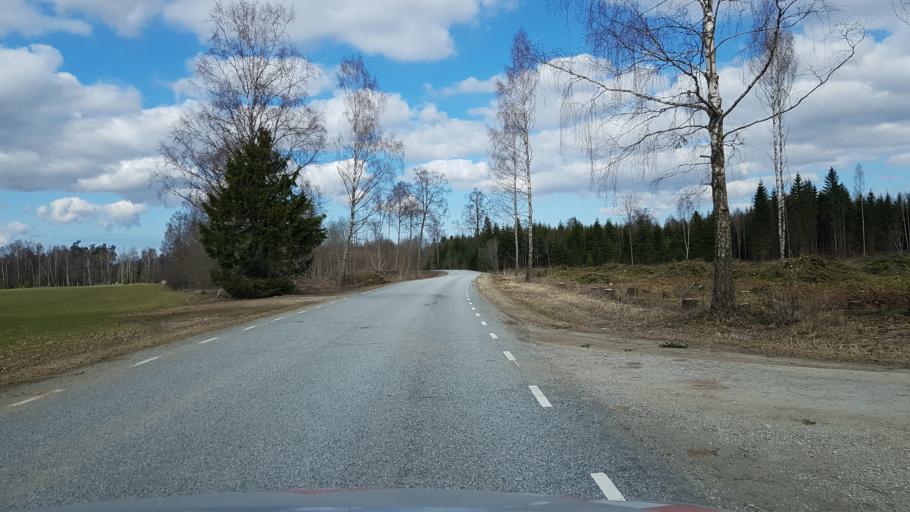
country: EE
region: Laeaene-Virumaa
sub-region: Tamsalu vald
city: Tamsalu
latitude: 59.2201
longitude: 26.1607
